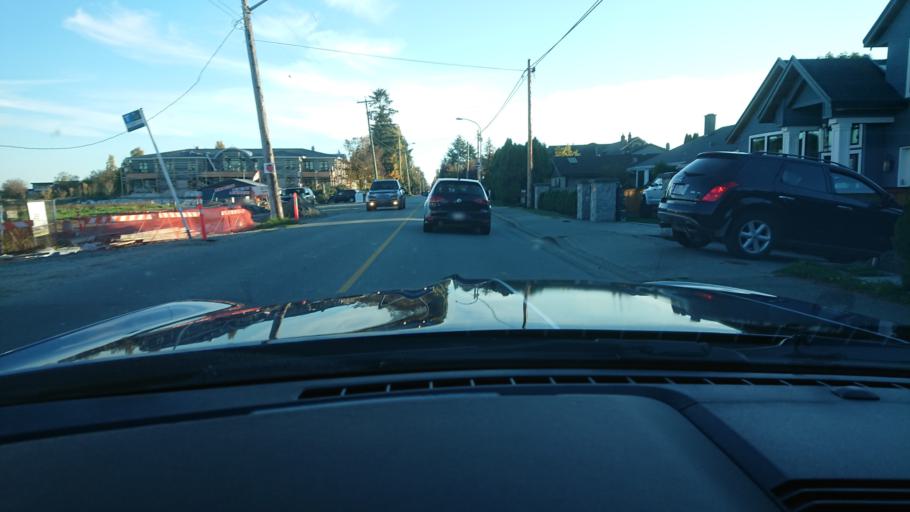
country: CA
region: British Columbia
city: Richmond
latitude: 49.1302
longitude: -123.1589
